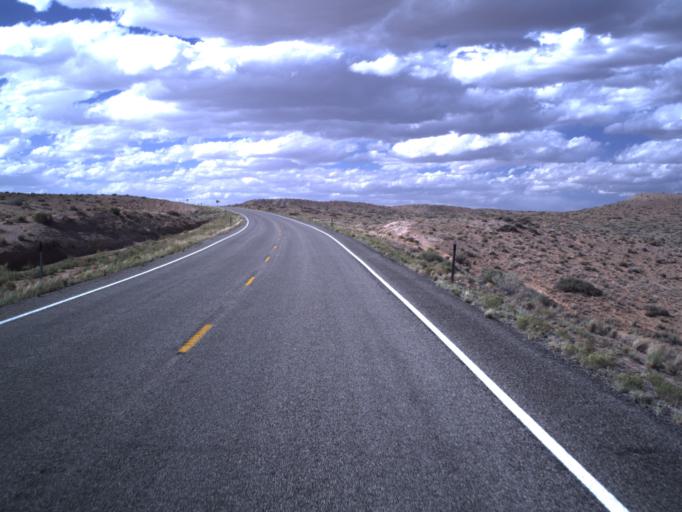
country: US
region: Utah
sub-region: Emery County
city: Ferron
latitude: 38.3323
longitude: -110.6816
